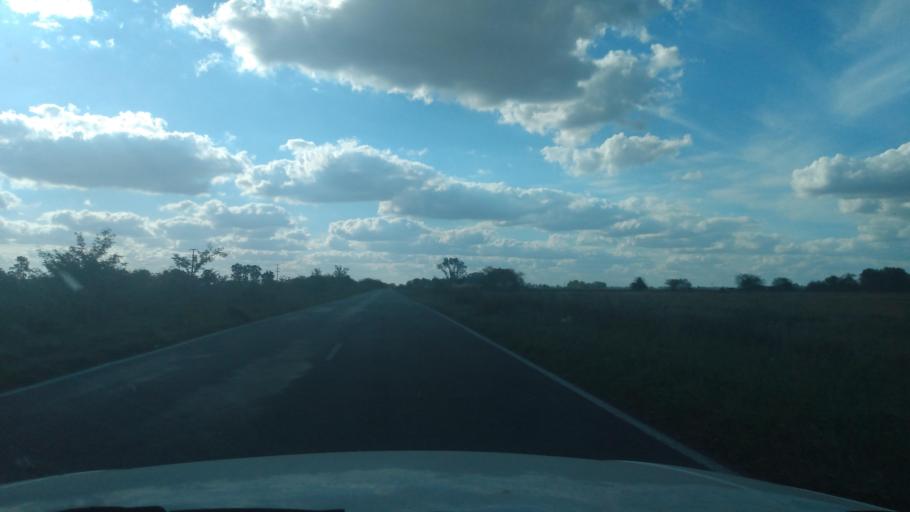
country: AR
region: Buenos Aires
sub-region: Partido de Mercedes
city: Mercedes
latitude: -34.7728
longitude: -59.3702
